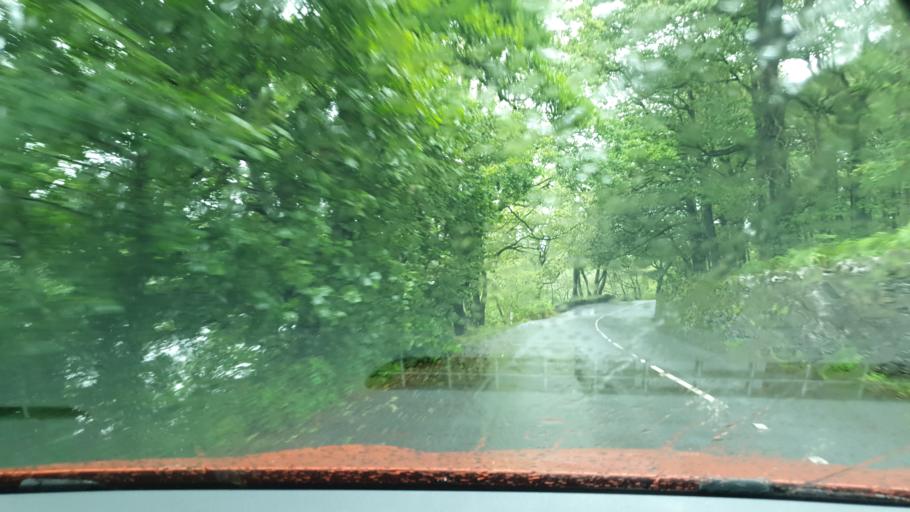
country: GB
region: England
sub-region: Cumbria
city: Ulverston
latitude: 54.3164
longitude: -3.0917
